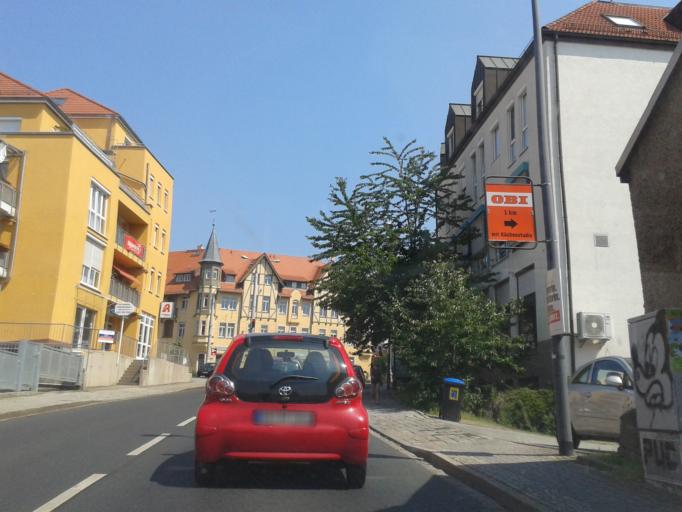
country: DE
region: Saxony
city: Radeberg
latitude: 51.0611
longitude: 13.8478
